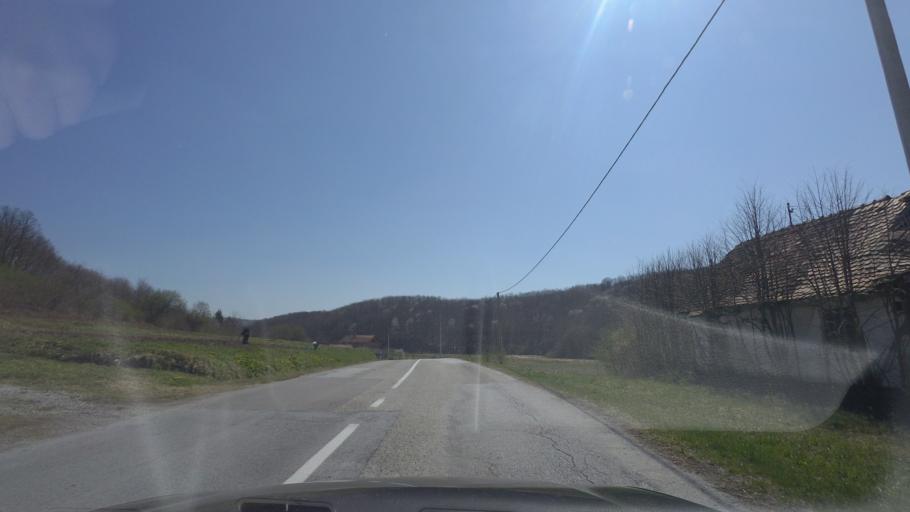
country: HR
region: Karlovacka
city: Vojnic
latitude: 45.3709
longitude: 15.6533
